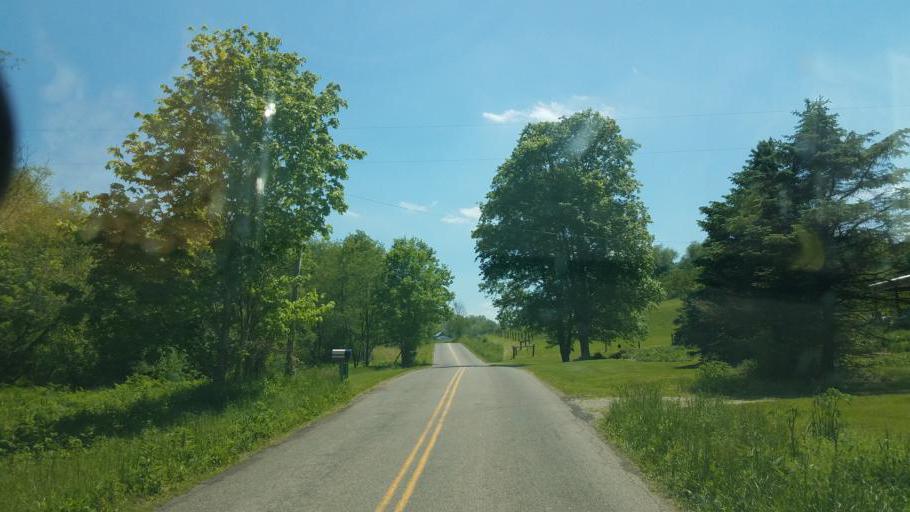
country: US
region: Ohio
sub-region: Licking County
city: Utica
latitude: 40.2450
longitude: -82.2844
